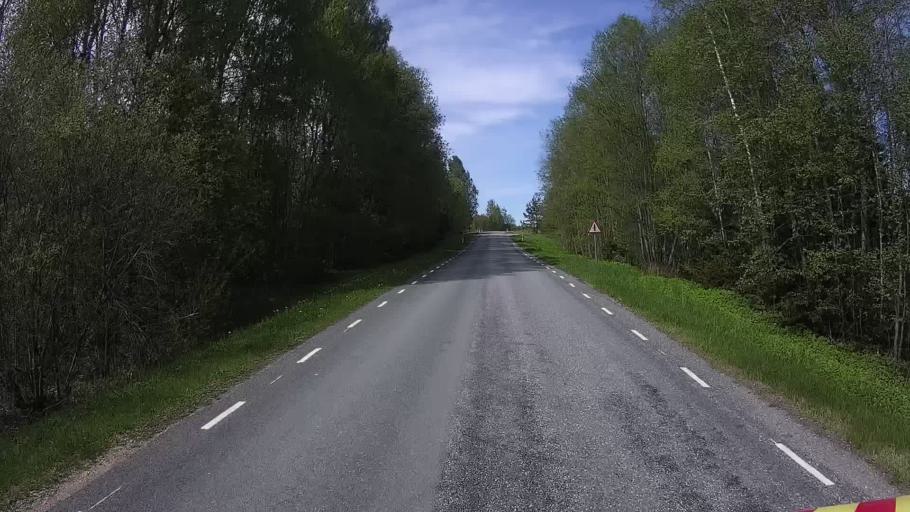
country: EE
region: Valgamaa
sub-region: Valga linn
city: Valga
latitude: 57.6559
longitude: 26.2932
